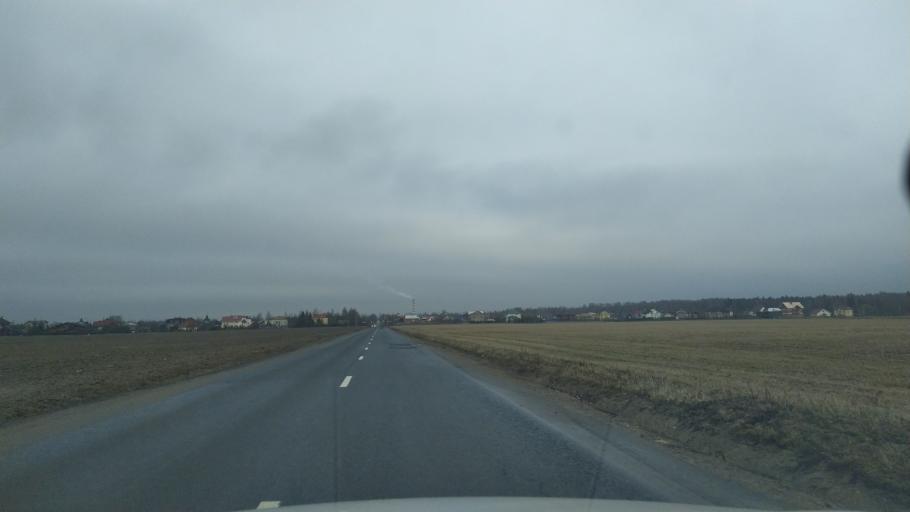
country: RU
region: St.-Petersburg
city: Aleksandrovskaya
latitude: 59.7185
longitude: 30.3407
